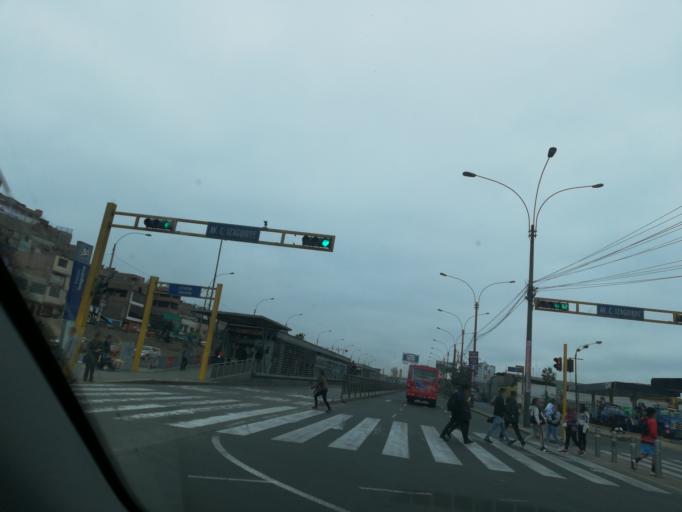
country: PE
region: Lima
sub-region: Lima
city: Independencia
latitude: -11.9890
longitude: -77.0571
